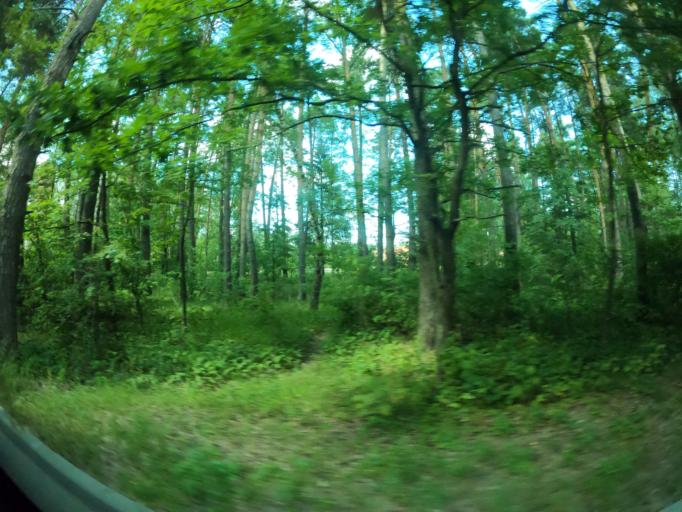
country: RU
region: Moskovskaya
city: Protvino
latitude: 54.8731
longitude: 37.2259
